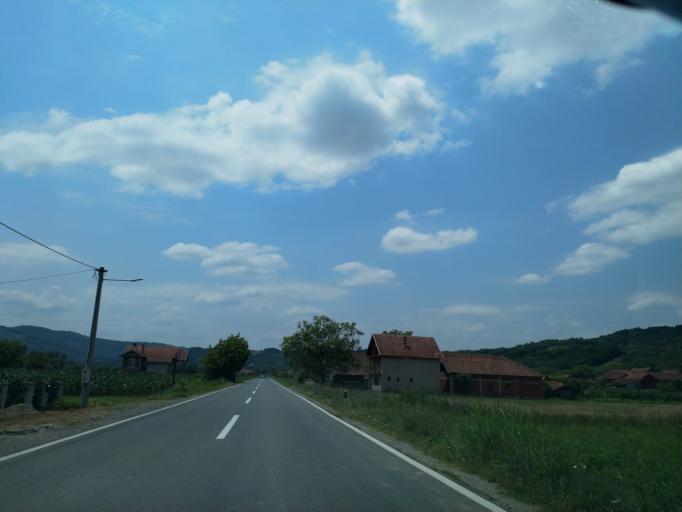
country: RS
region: Central Serbia
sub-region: Toplicki Okrug
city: Blace
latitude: 43.4393
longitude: 21.2211
